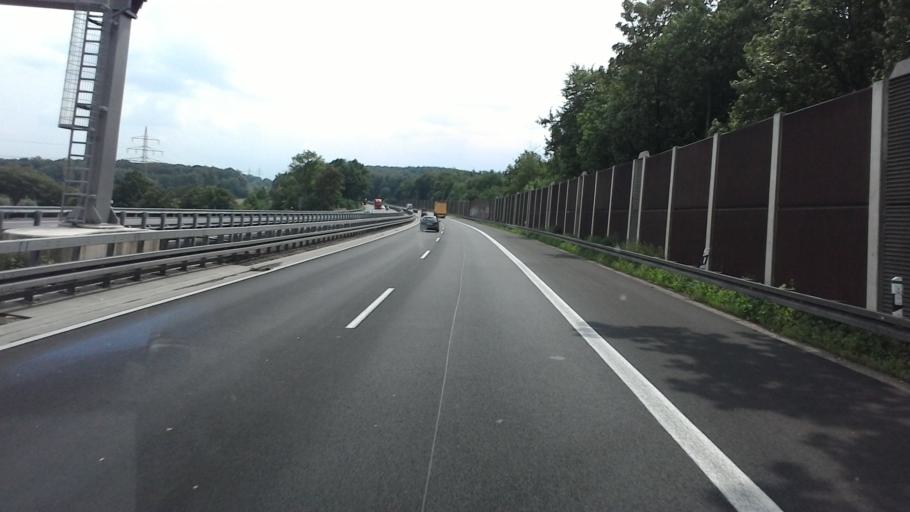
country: DE
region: North Rhine-Westphalia
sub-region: Regierungsbezirk Koln
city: Wurselen
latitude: 50.7949
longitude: 6.1692
